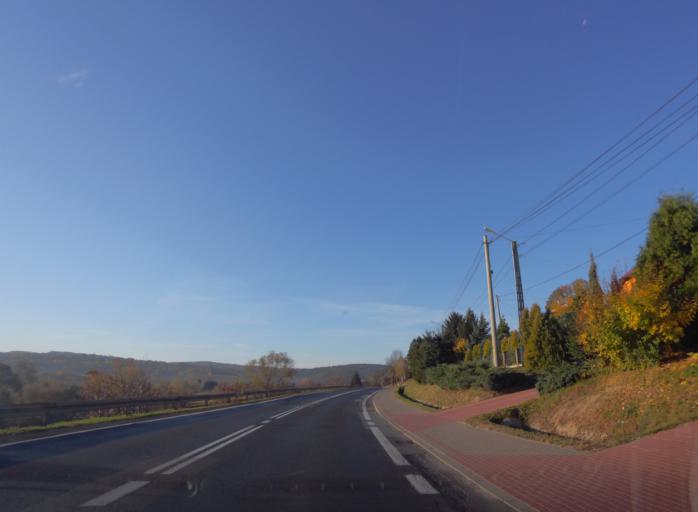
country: PL
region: Subcarpathian Voivodeship
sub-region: Powiat rzeszowski
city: Lubenia
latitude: 49.9436
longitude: 21.9102
